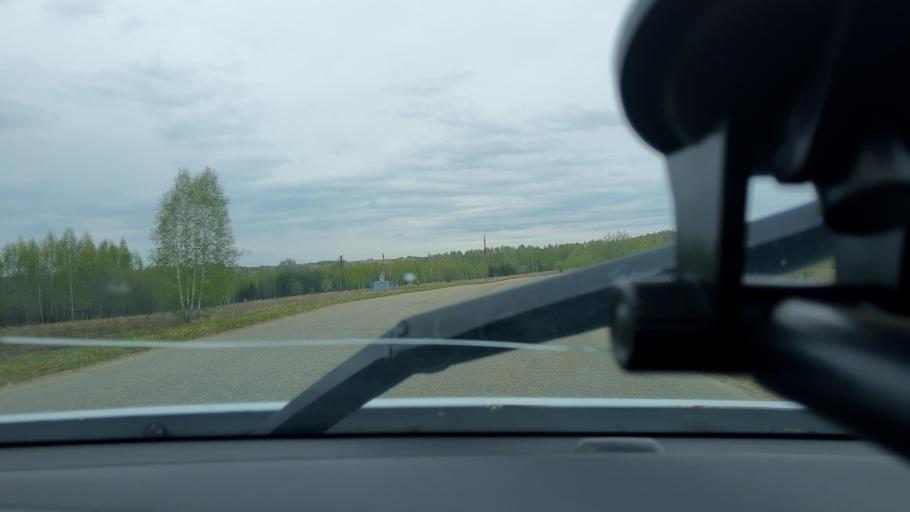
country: RU
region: Bashkortostan
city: Pavlovka
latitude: 55.3758
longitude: 56.4213
